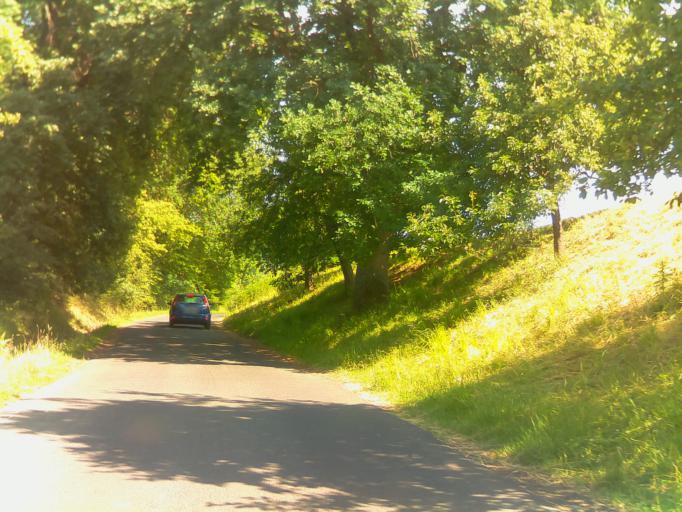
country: DE
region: Hesse
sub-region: Regierungsbezirk Giessen
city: Rabenau
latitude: 50.6814
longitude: 8.8232
